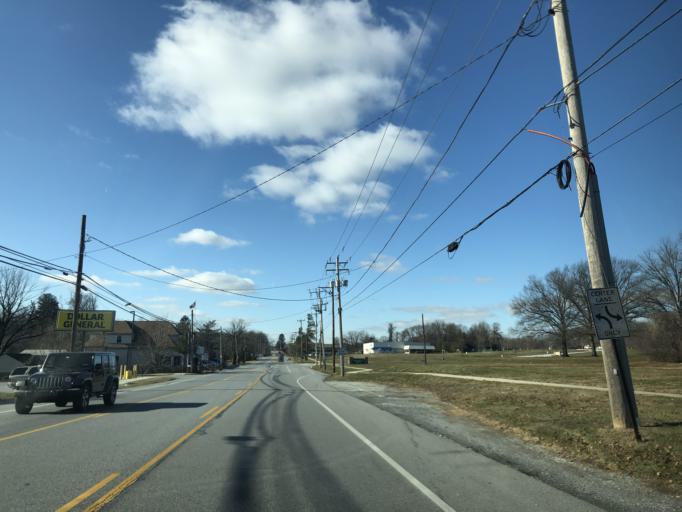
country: US
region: Pennsylvania
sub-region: Chester County
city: Coatesville
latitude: 39.9843
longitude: -75.8532
